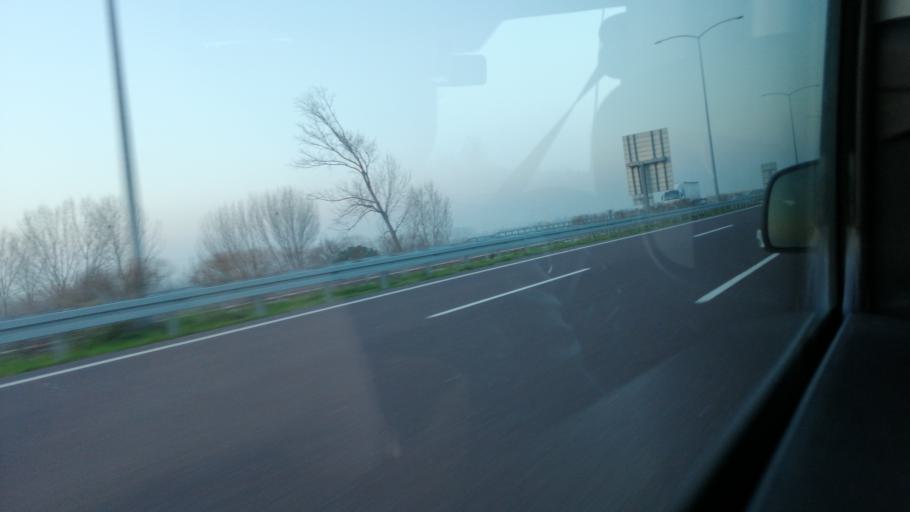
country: TR
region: Yalova
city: Altinova
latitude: 40.7037
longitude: 29.4919
